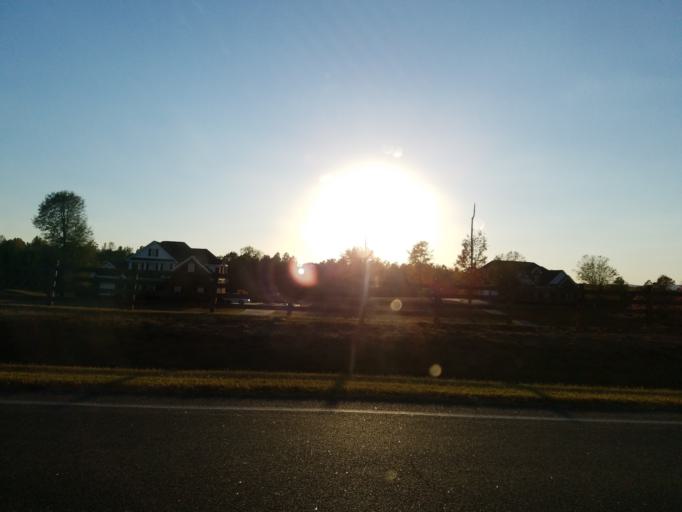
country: US
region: Georgia
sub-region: Gordon County
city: Calhoun
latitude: 34.5194
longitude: -84.9669
